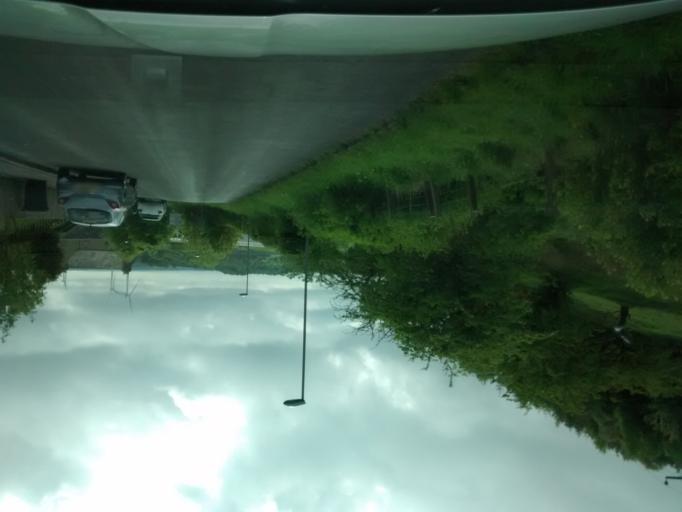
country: GB
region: Scotland
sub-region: North Lanarkshire
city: Harthill
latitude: 55.8857
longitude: -3.7638
